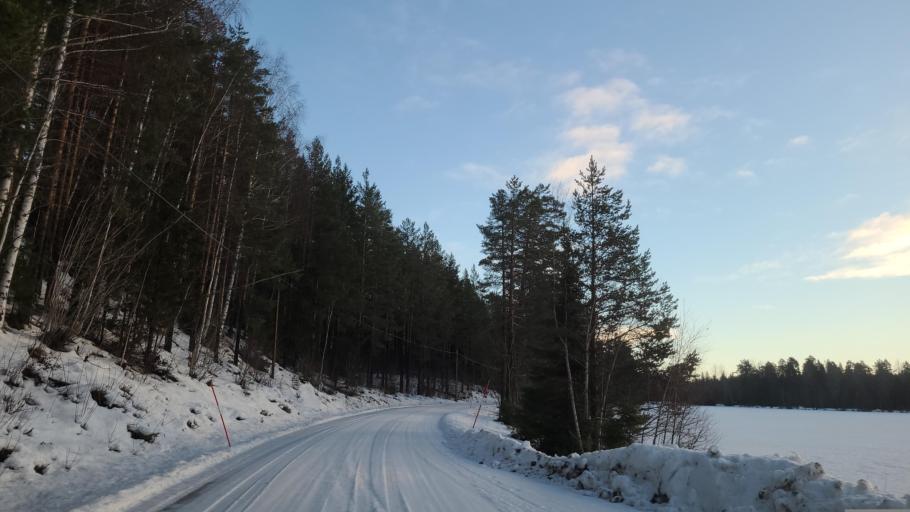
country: SE
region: Gaevleborg
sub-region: Bollnas Kommun
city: Kilafors
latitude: 61.3884
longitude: 16.6876
